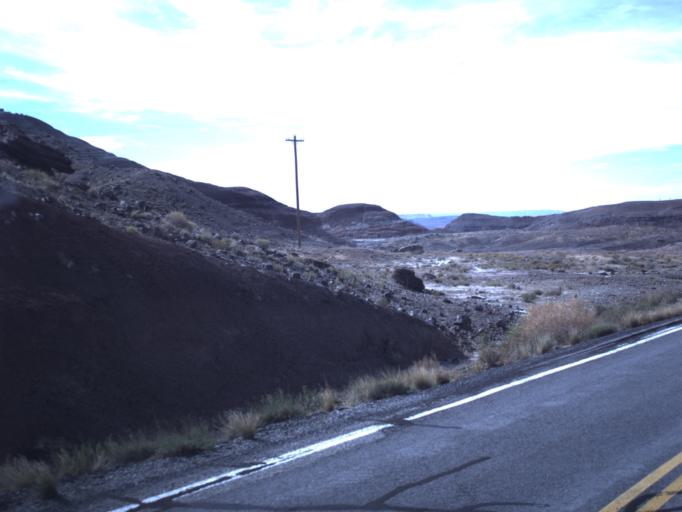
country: US
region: Utah
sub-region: San Juan County
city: Blanding
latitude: 37.3263
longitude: -109.3190
